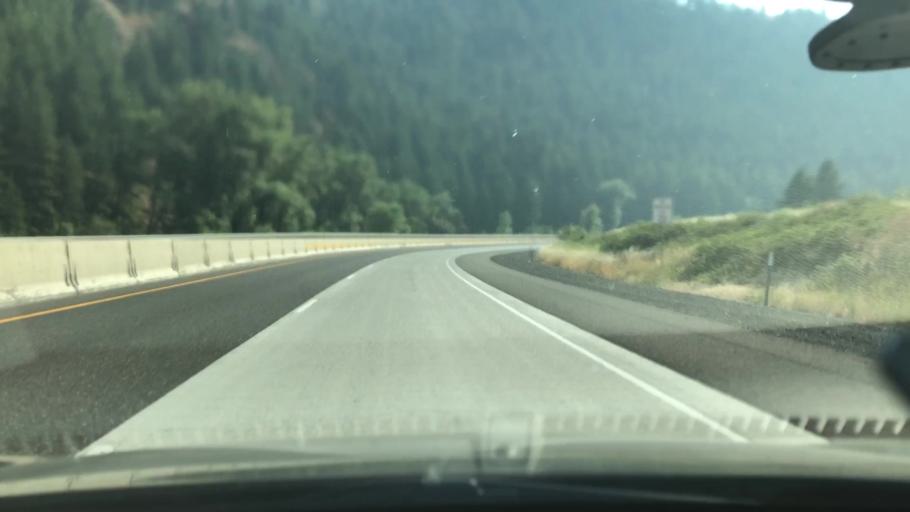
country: US
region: Oregon
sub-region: Union County
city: La Grande
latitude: 45.3490
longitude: -118.2000
